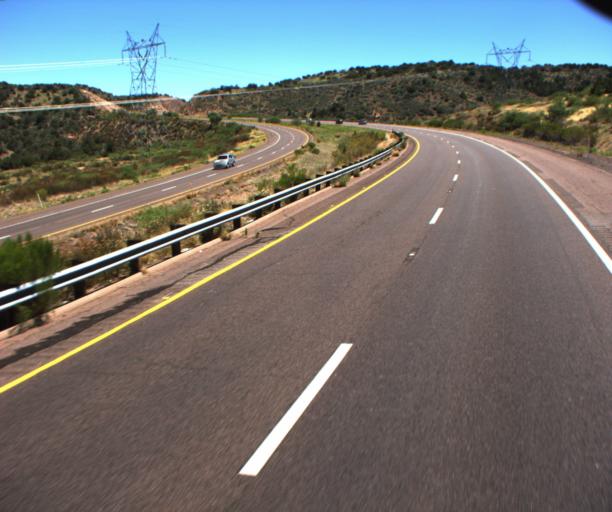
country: US
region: Arizona
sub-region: Gila County
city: Tonto Basin
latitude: 34.0134
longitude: -111.3599
